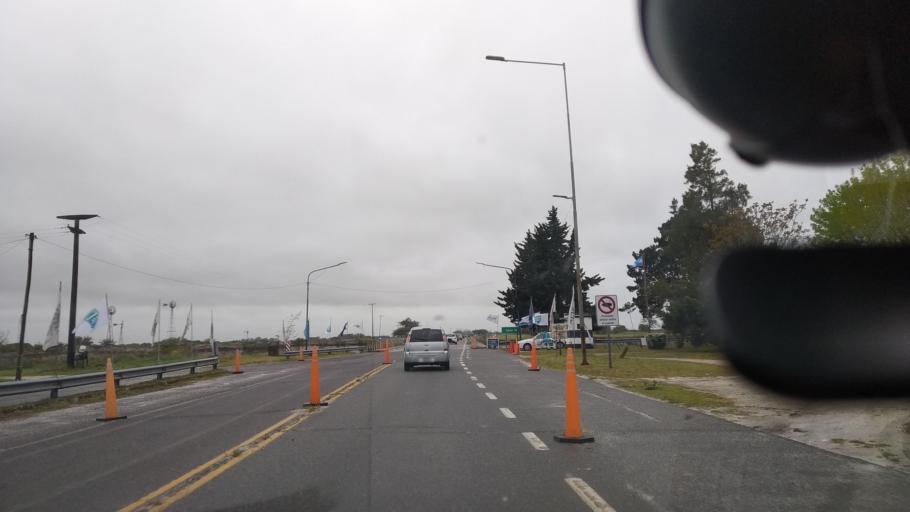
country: AR
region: Buenos Aires
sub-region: Partido de Castelli
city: Castelli
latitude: -35.9738
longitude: -57.4496
